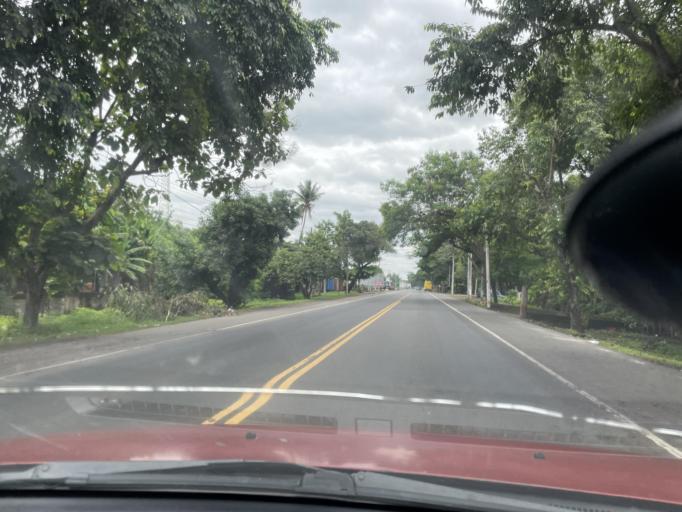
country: SV
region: San Miguel
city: El Transito
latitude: 13.3461
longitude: -88.3458
